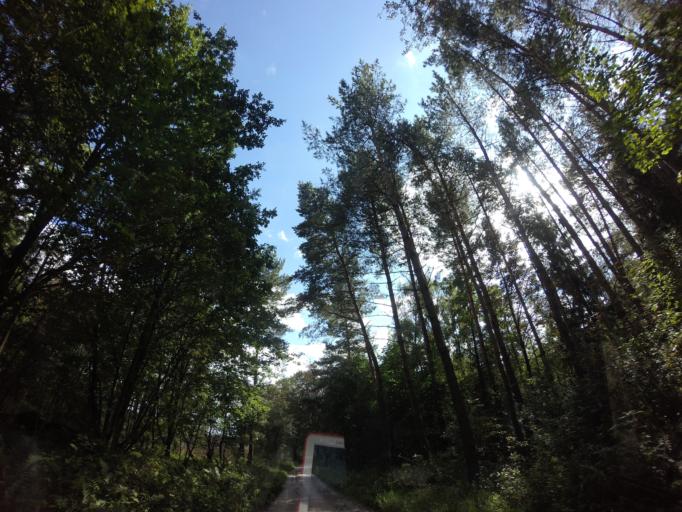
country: PL
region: West Pomeranian Voivodeship
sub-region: Powiat choszczenski
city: Recz
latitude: 53.2921
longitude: 15.5975
